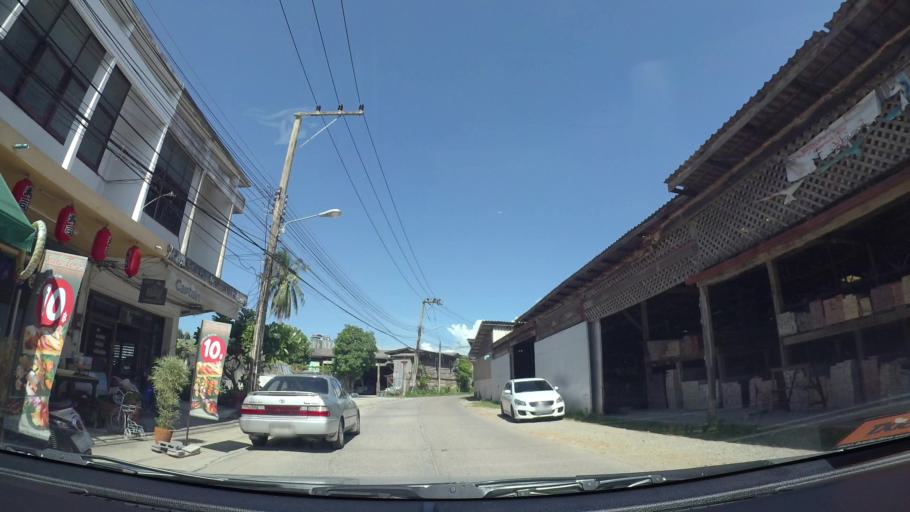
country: TH
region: Chon Buri
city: Si Racha
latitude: 13.1636
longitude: 100.9319
